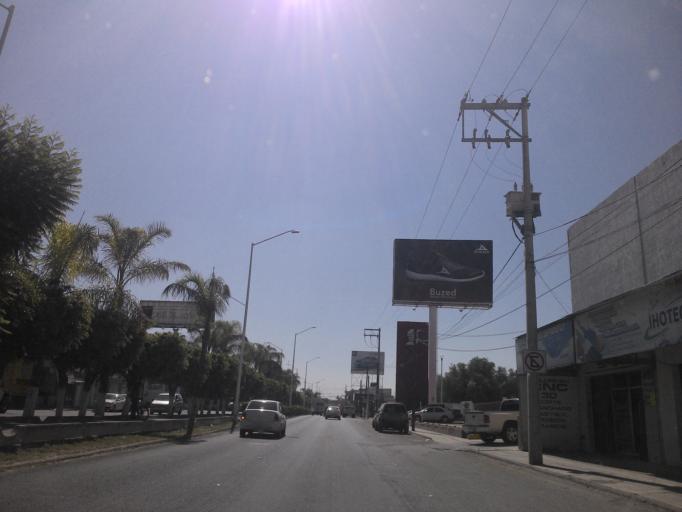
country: MX
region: Guanajuato
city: San Francisco del Rincon
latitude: 21.0288
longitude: -101.8579
